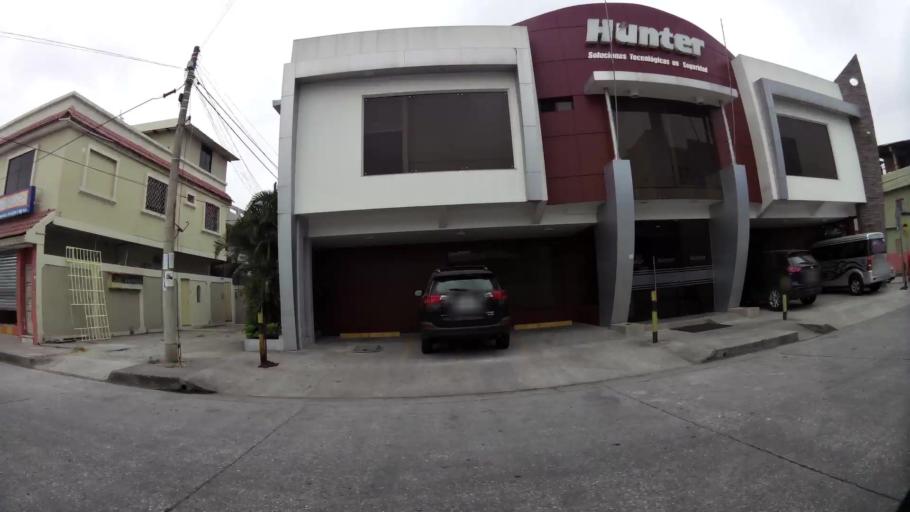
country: EC
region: Guayas
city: Eloy Alfaro
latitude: -2.1530
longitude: -79.8928
